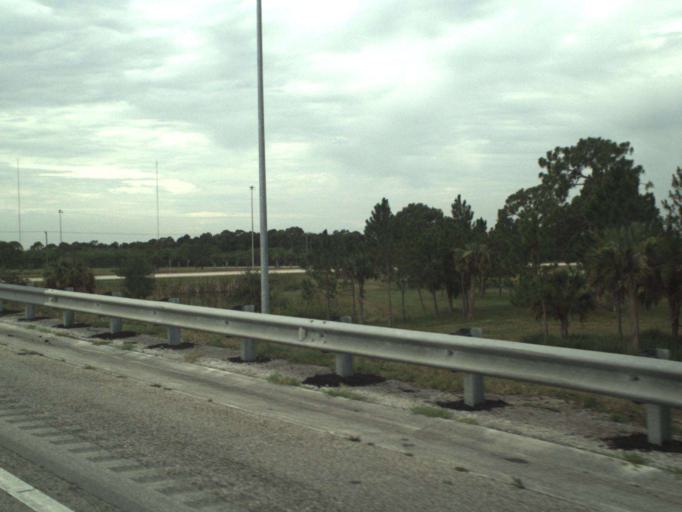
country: US
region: Florida
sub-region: Martin County
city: Palm City
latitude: 27.1638
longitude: -80.3918
